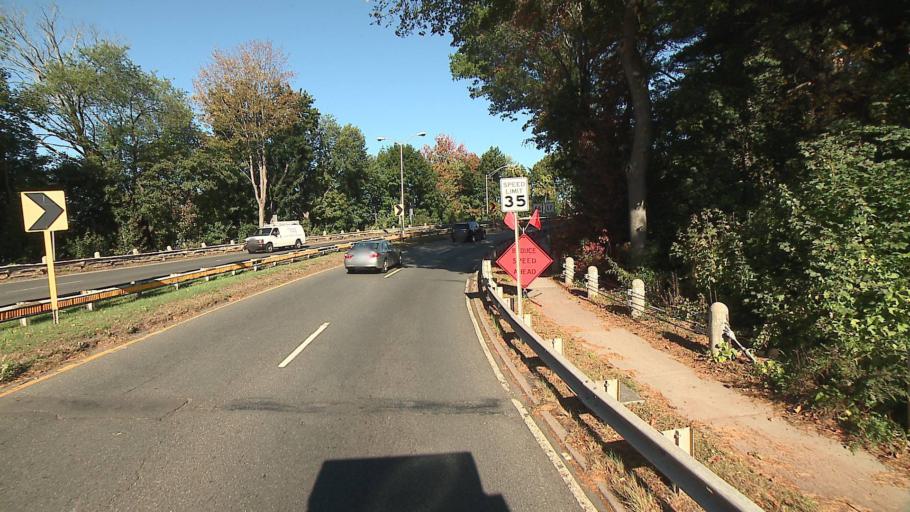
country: US
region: Connecticut
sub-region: Middlesex County
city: Middletown
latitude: 41.5667
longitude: -72.6542
